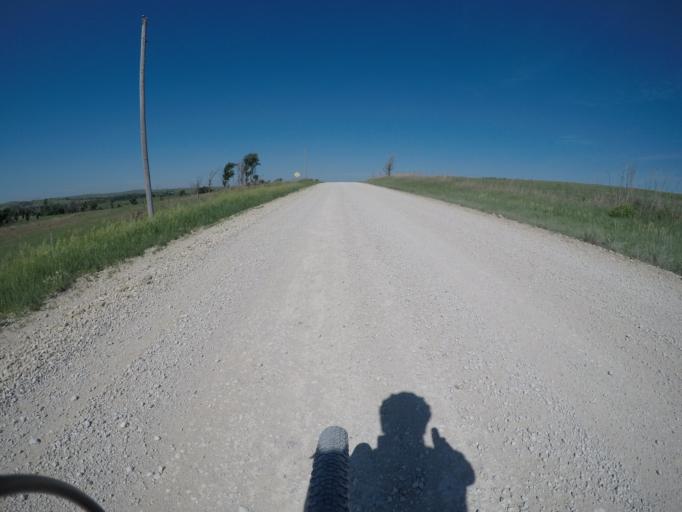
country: US
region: Kansas
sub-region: Wabaunsee County
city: Alma
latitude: 39.0153
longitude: -96.1175
